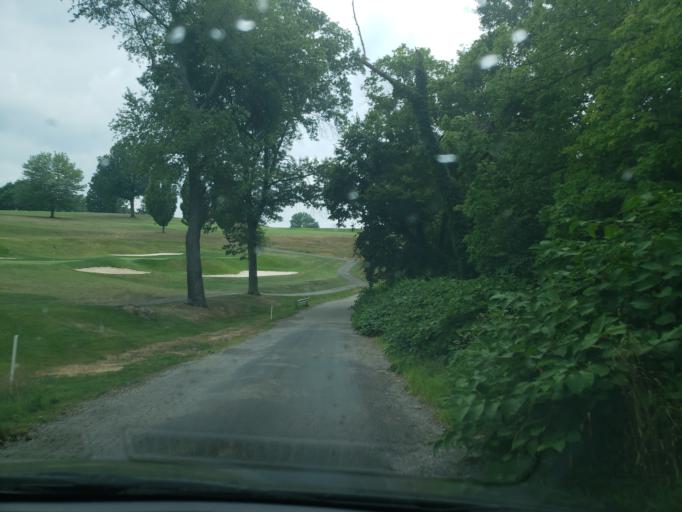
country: US
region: Pennsylvania
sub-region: Allegheny County
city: Avalon
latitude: 40.5153
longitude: -80.0639
